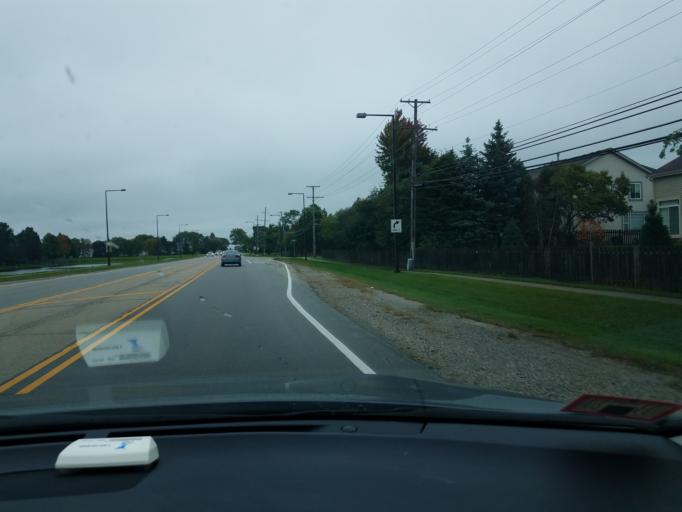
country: US
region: Illinois
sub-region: Cook County
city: Buffalo Grove
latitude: 42.1865
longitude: -87.9554
